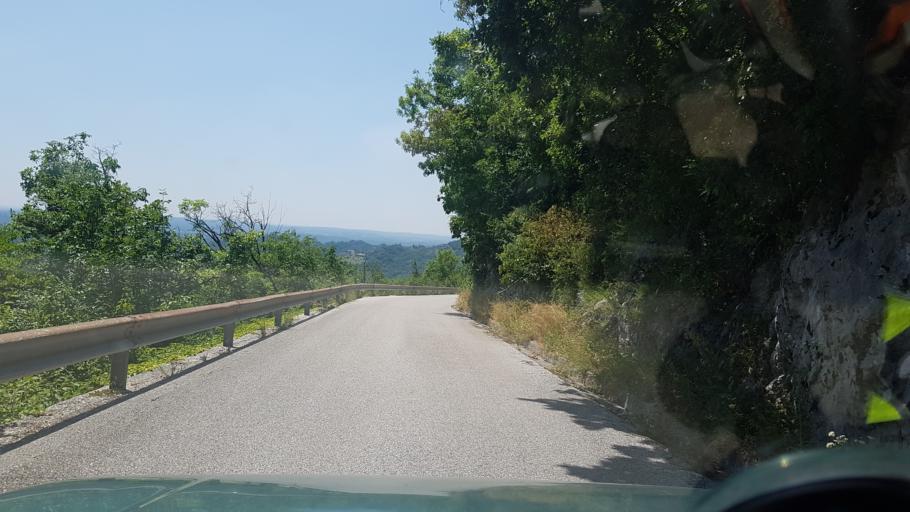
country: IT
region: Friuli Venezia Giulia
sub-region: Provincia di Udine
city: Nimis
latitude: 46.2226
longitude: 13.2718
